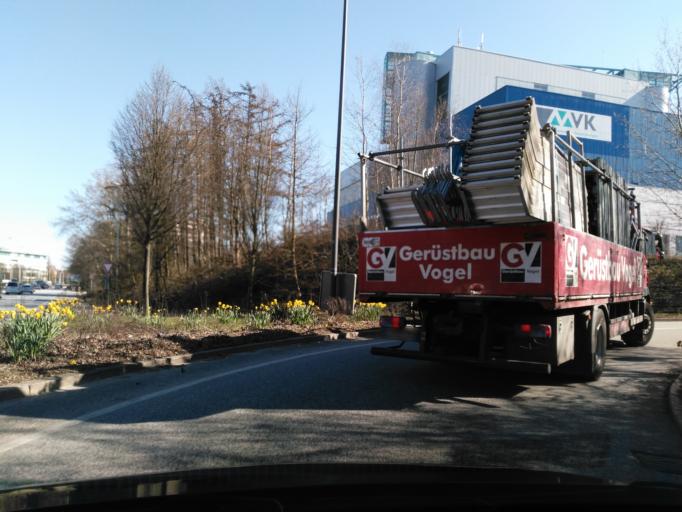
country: DE
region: Schleswig-Holstein
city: Kiel
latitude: 54.3082
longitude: 10.1121
